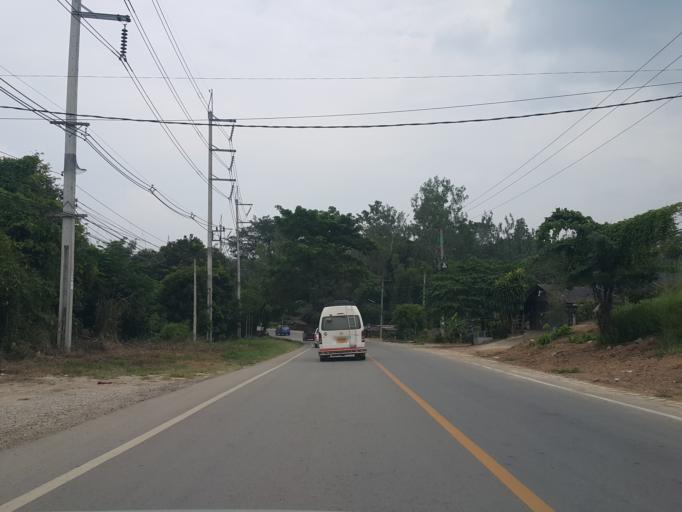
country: TH
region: Chiang Mai
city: Mae Taeng
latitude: 19.0894
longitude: 98.8889
